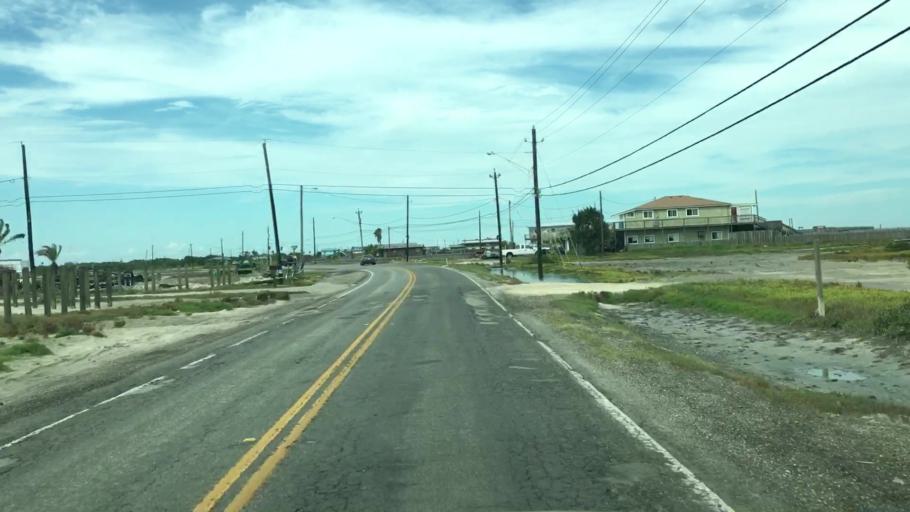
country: US
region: Texas
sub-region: Nueces County
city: Corpus Christi
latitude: 27.6355
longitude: -97.2882
